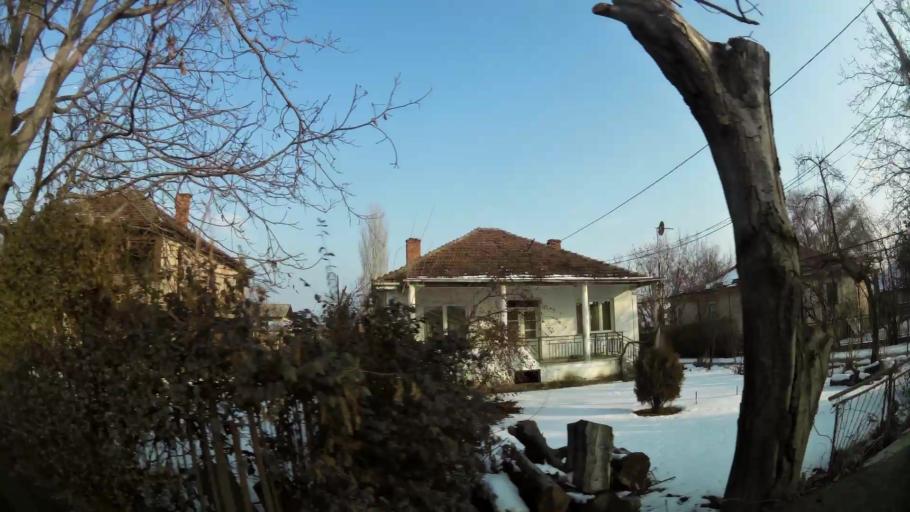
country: MK
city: Creshevo
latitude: 42.0242
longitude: 21.5149
